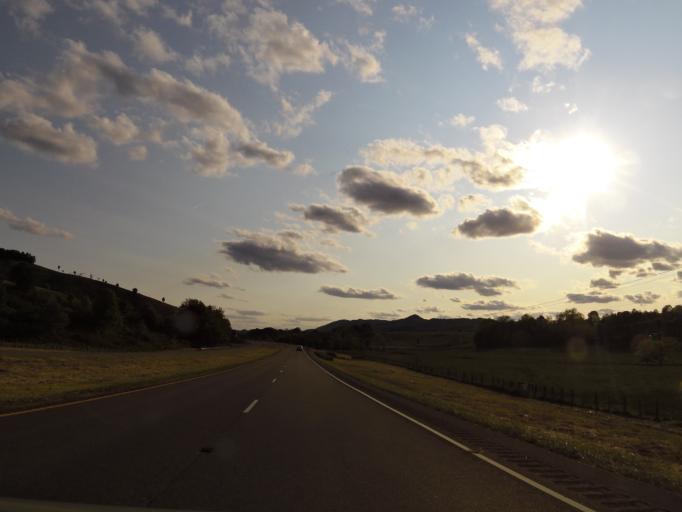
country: US
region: Virginia
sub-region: Russell County
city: Honaker
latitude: 36.9678
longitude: -81.9130
